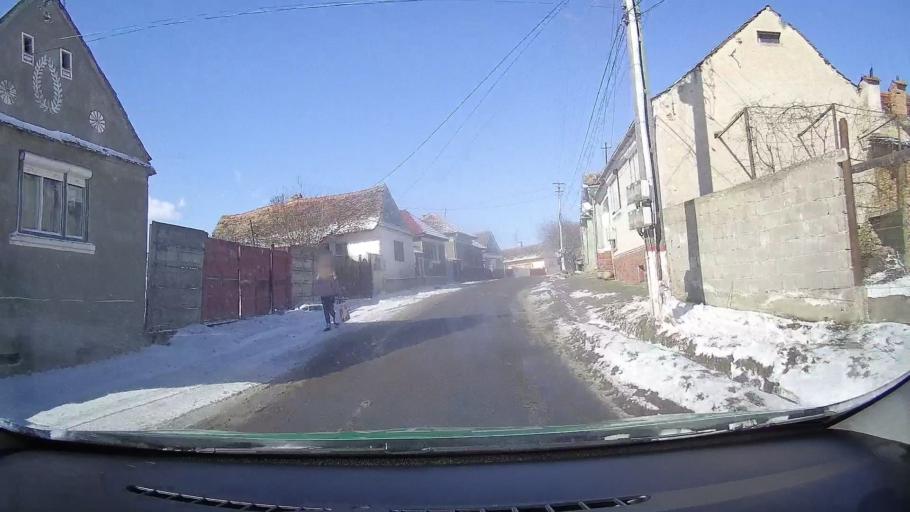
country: RO
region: Sibiu
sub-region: Comuna Avrig
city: Avrig
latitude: 45.7579
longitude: 24.3903
